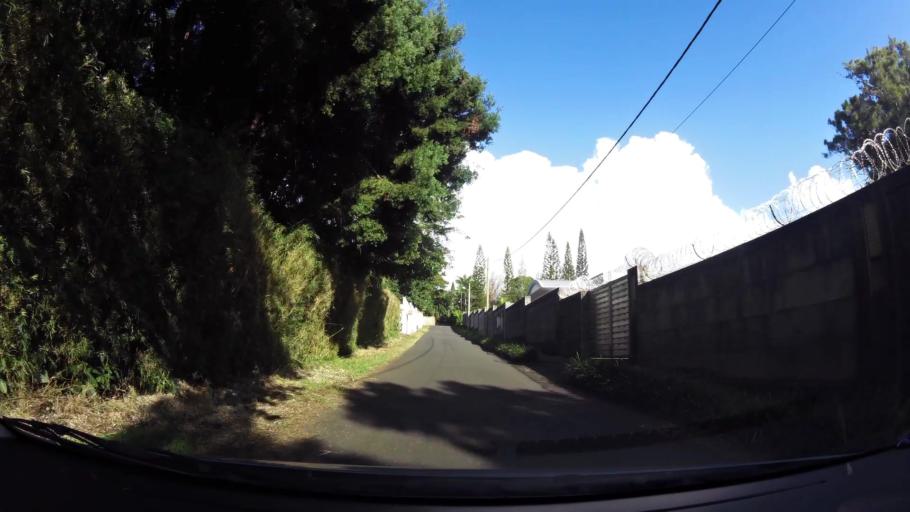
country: MU
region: Plaines Wilhems
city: Curepipe
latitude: -20.3104
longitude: 57.5013
